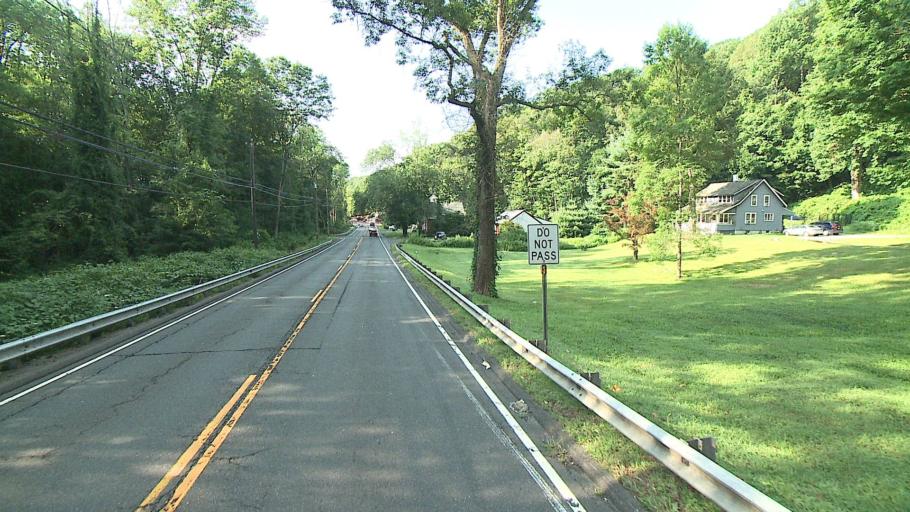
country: US
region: Connecticut
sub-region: Fairfield County
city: Georgetown
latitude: 41.2469
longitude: -73.4344
